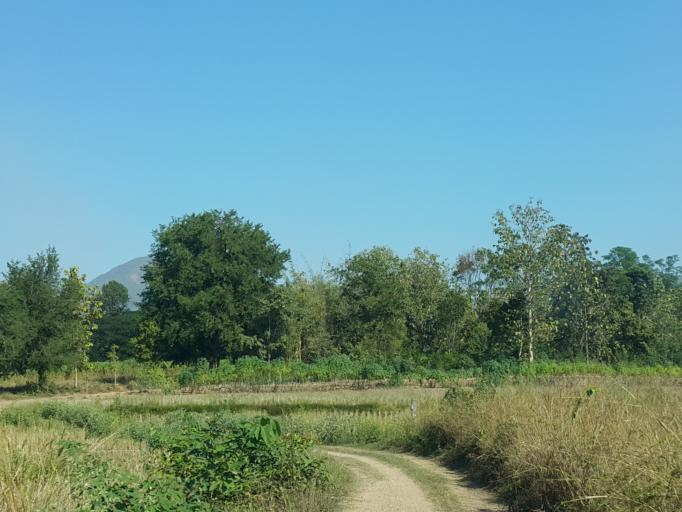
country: TH
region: Sukhothai
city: Thung Saliam
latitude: 17.3276
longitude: 99.4608
